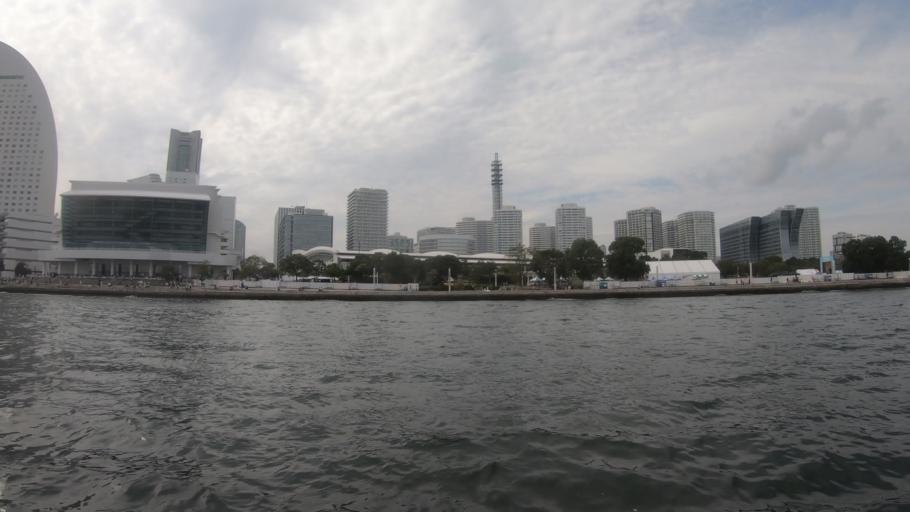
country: JP
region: Kanagawa
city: Yokohama
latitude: 35.4602
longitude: 139.6392
